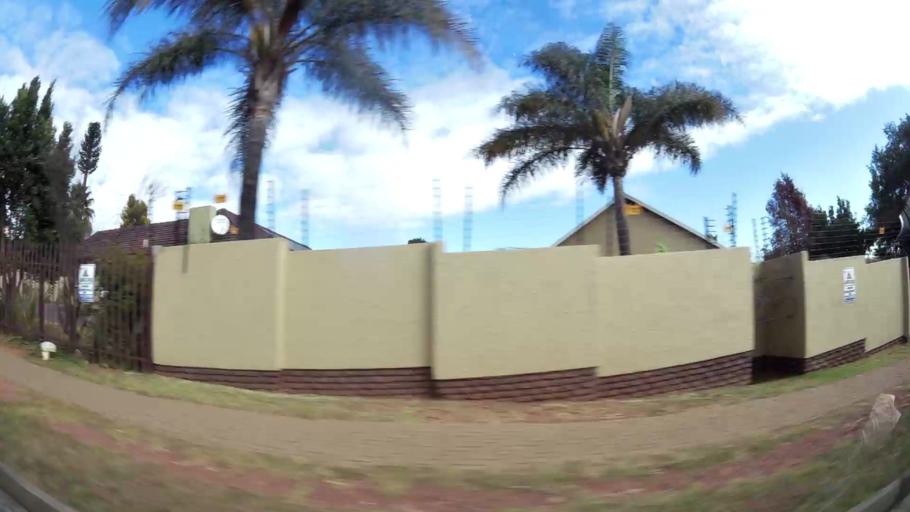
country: ZA
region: Gauteng
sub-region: City of Johannesburg Metropolitan Municipality
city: Roodepoort
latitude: -26.1176
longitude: 27.8508
